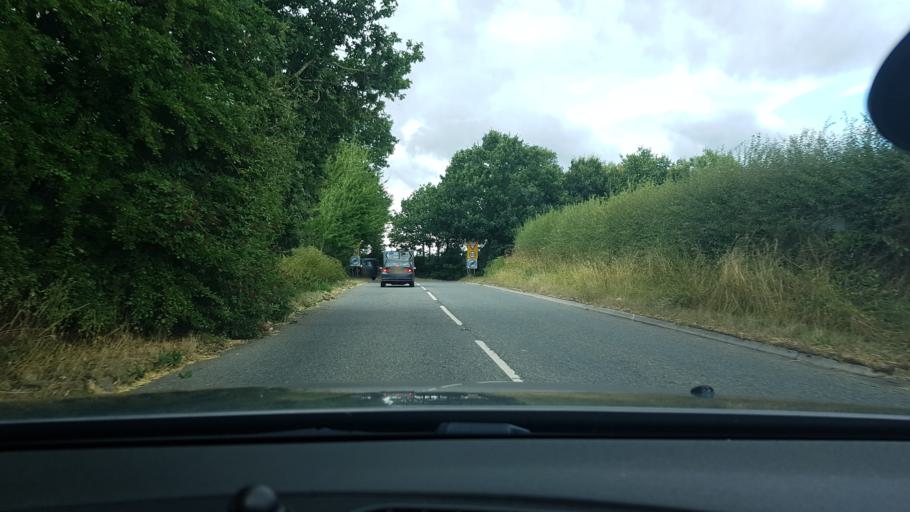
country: GB
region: England
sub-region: West Berkshire
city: Wickham
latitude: 51.4582
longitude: -1.4734
